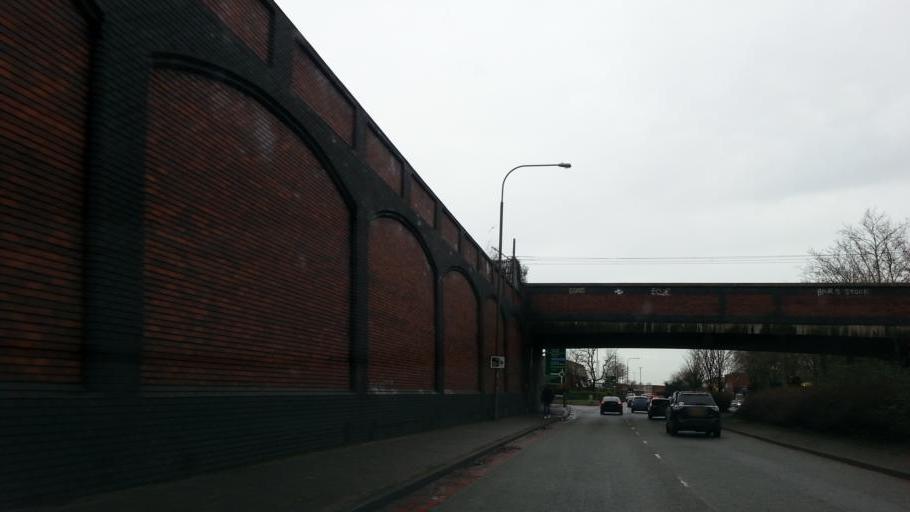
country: GB
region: England
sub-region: City and Borough of Birmingham
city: Hockley
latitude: 52.4898
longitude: -1.9168
